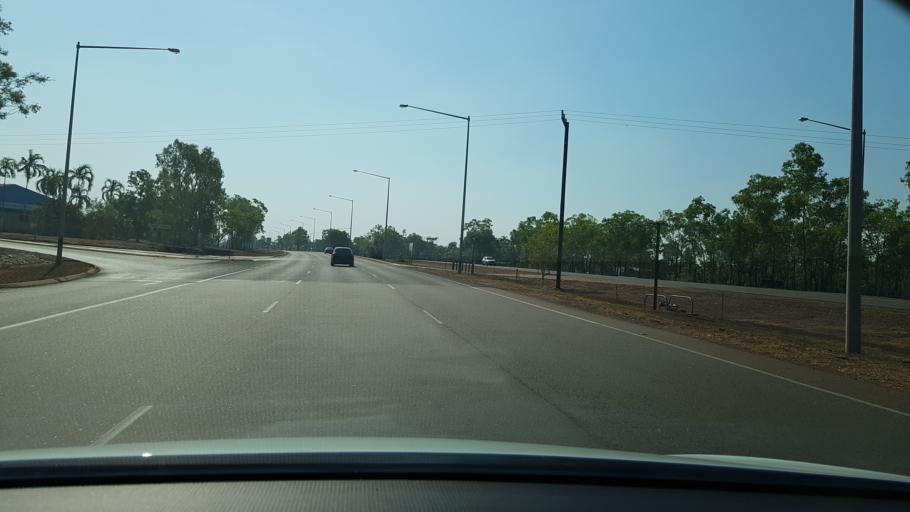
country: AU
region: Northern Territory
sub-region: Palmerston
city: Palmerston
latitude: -12.4623
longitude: 130.9739
